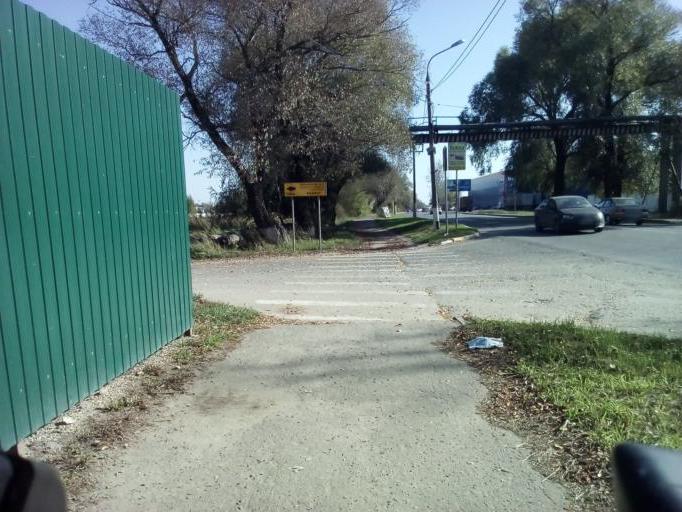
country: RU
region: Moskovskaya
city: Ramenskoye
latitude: 55.5556
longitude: 38.2653
